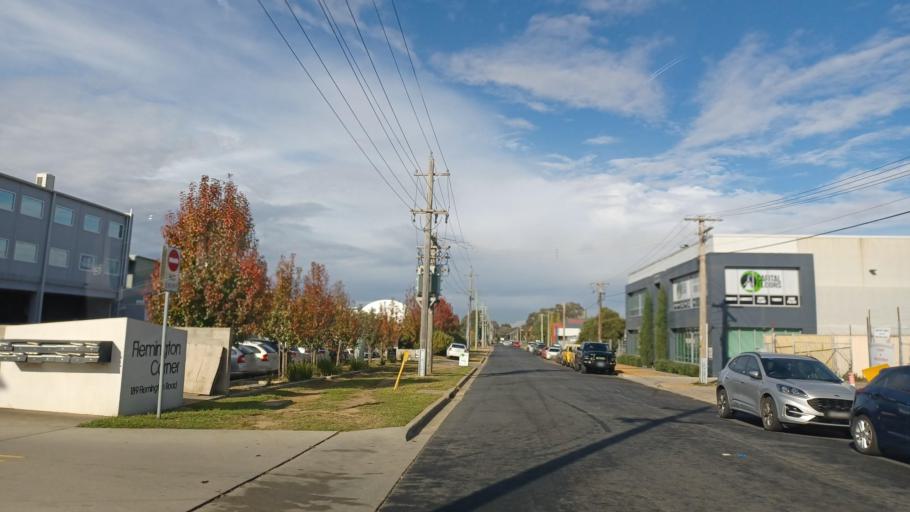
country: AU
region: Australian Capital Territory
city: Kaleen
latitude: -35.2163
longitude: 149.1443
